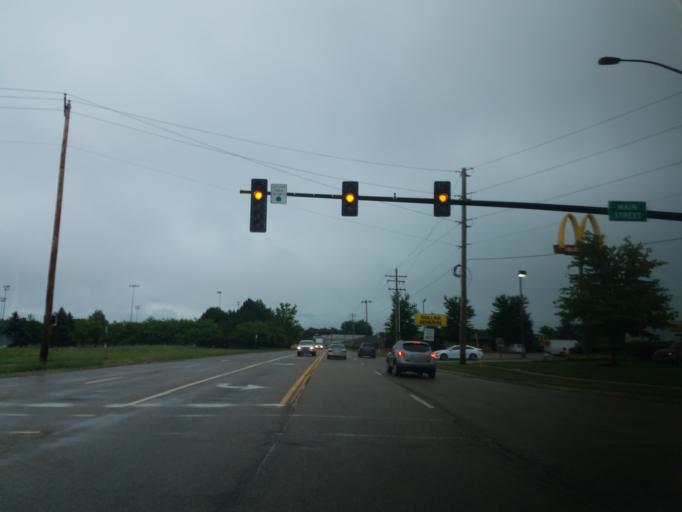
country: US
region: Illinois
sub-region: McLean County
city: Bloomington
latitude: 40.4500
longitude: -88.9922
